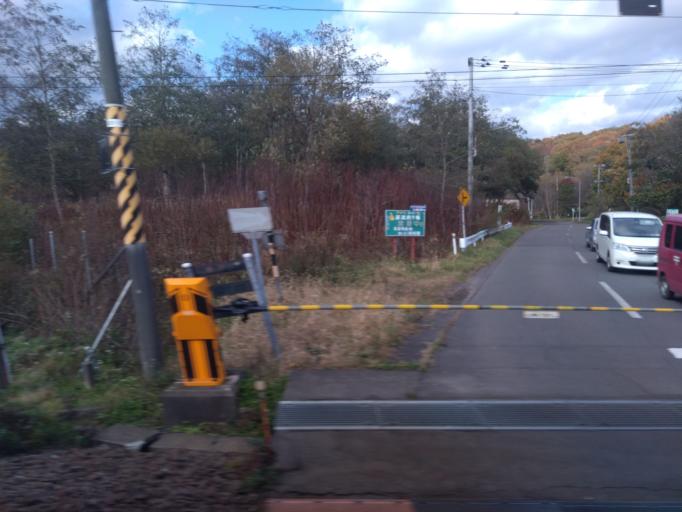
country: JP
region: Hokkaido
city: Shiraoi
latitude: 42.4613
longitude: 141.2070
